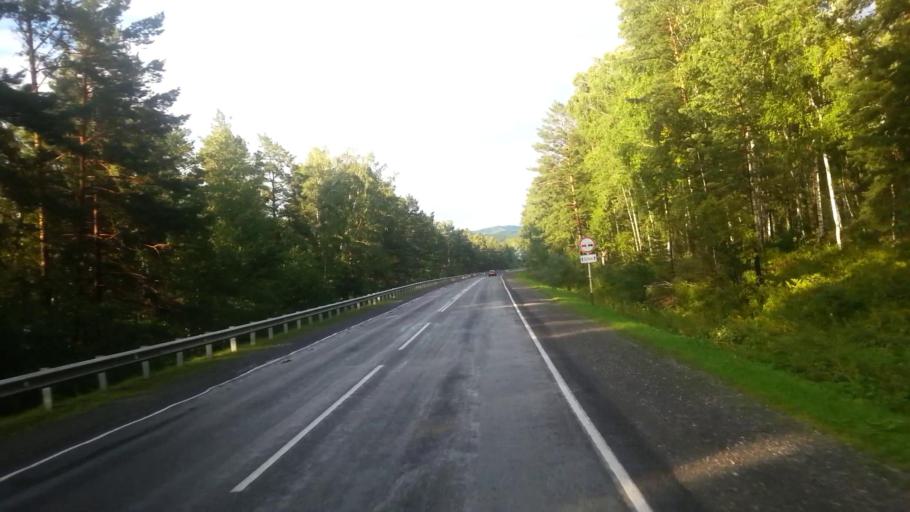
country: RU
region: Altay
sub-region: Mayminskiy Rayon
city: Manzherok
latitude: 51.8089
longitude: 85.7564
